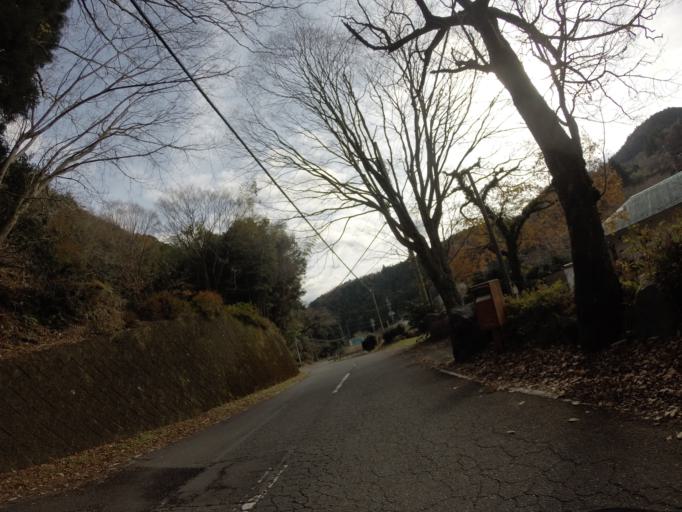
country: JP
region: Shizuoka
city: Heda
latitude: 34.8938
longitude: 138.8816
